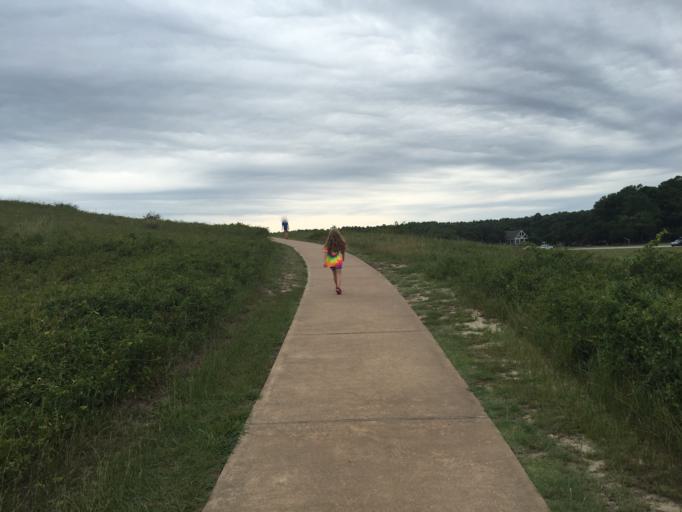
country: US
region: North Carolina
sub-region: Dare County
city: Kill Devil Hills
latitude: 36.0155
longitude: -75.6684
